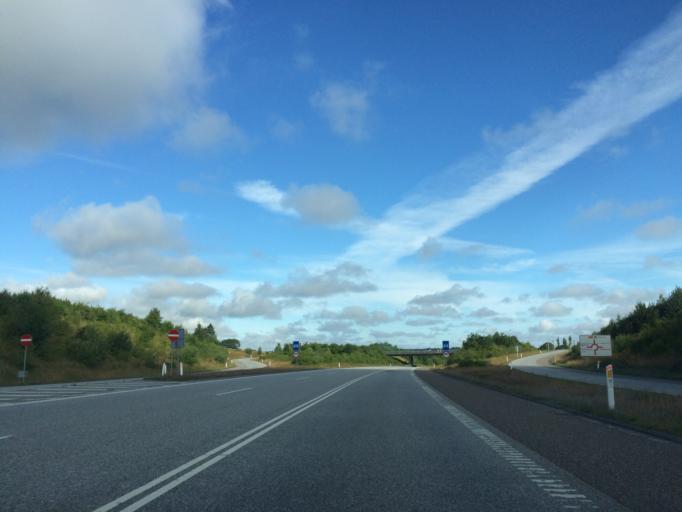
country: DK
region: Central Jutland
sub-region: Silkeborg Kommune
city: Kjellerup
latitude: 56.3379
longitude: 9.5374
